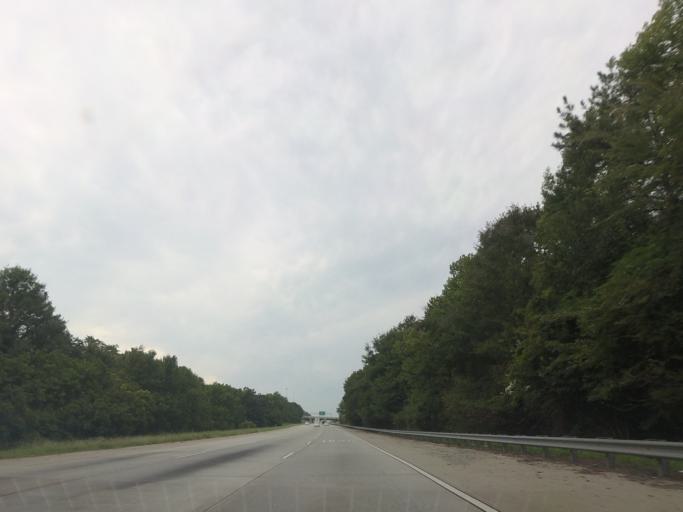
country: US
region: Georgia
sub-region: Bibb County
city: Macon
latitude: 32.7631
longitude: -83.7052
